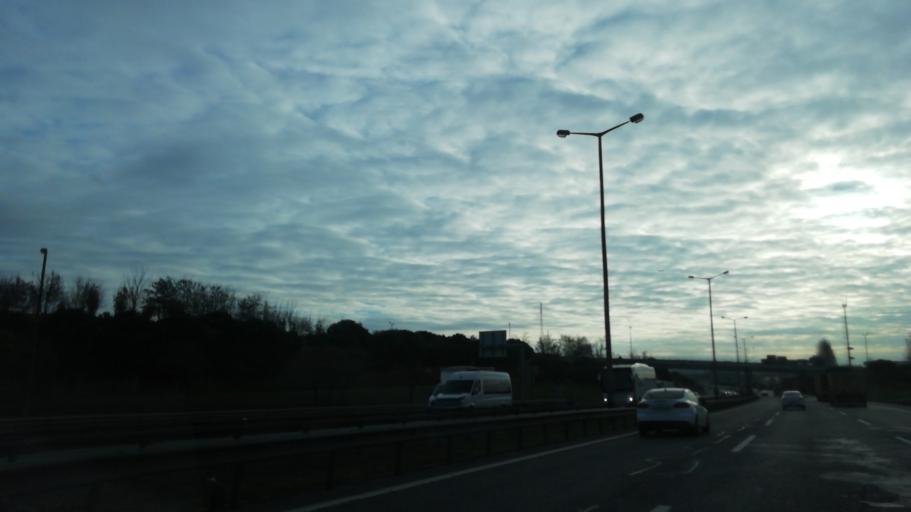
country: TR
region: Istanbul
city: Sultanbeyli
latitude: 40.9374
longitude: 29.3300
